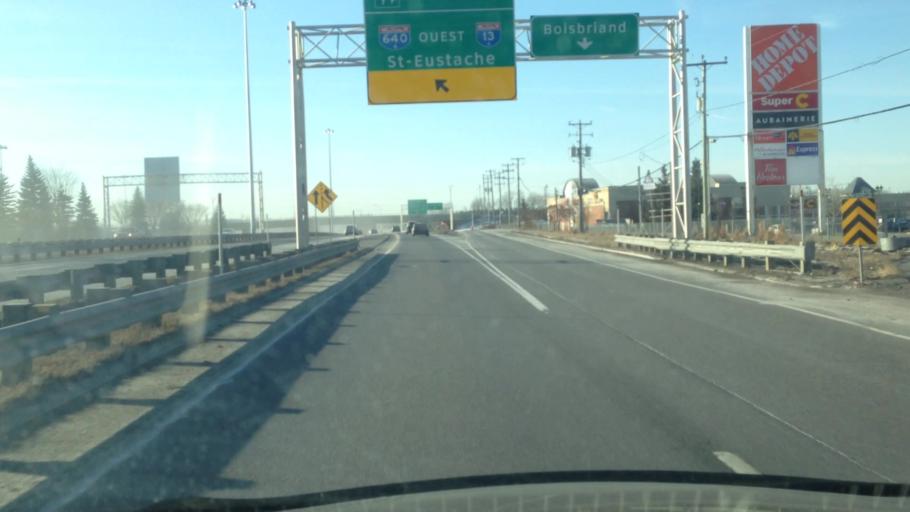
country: CA
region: Quebec
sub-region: Laurentides
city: Boisbriand
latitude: 45.6239
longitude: -73.8459
